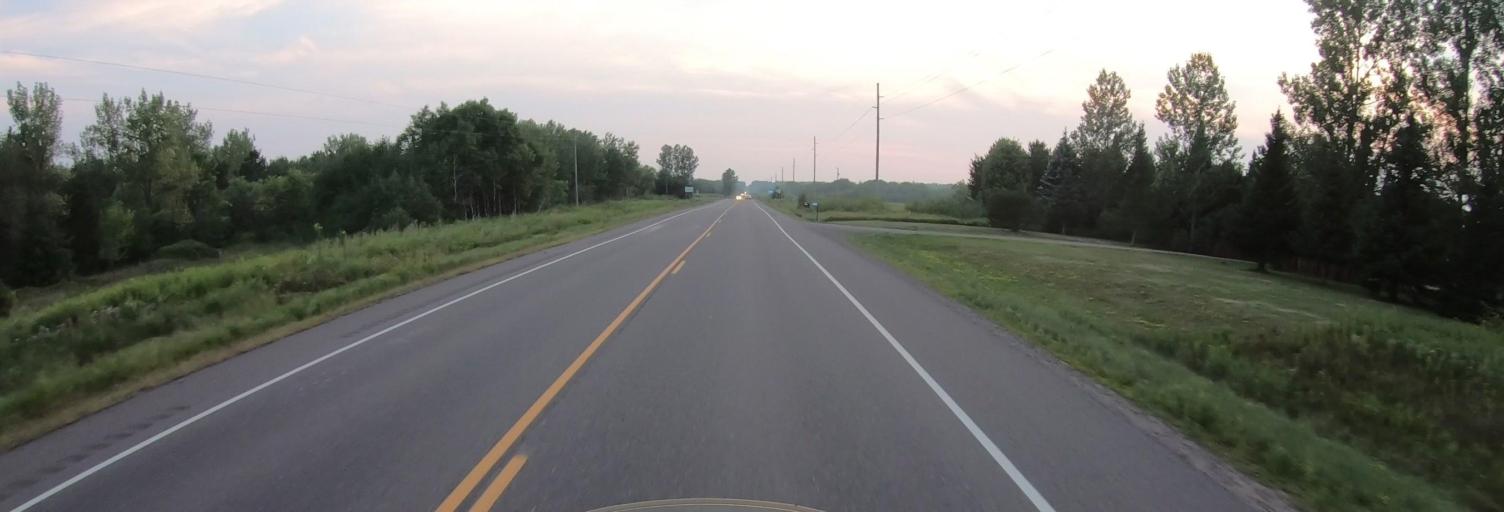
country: US
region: Wisconsin
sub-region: Burnett County
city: Grantsburg
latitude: 45.7736
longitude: -92.8140
